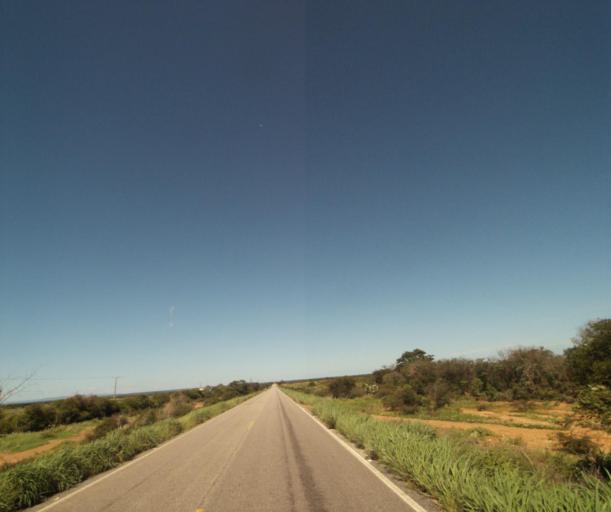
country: BR
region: Bahia
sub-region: Palmas De Monte Alto
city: Palmas de Monte Alto
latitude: -14.2563
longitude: -43.2467
